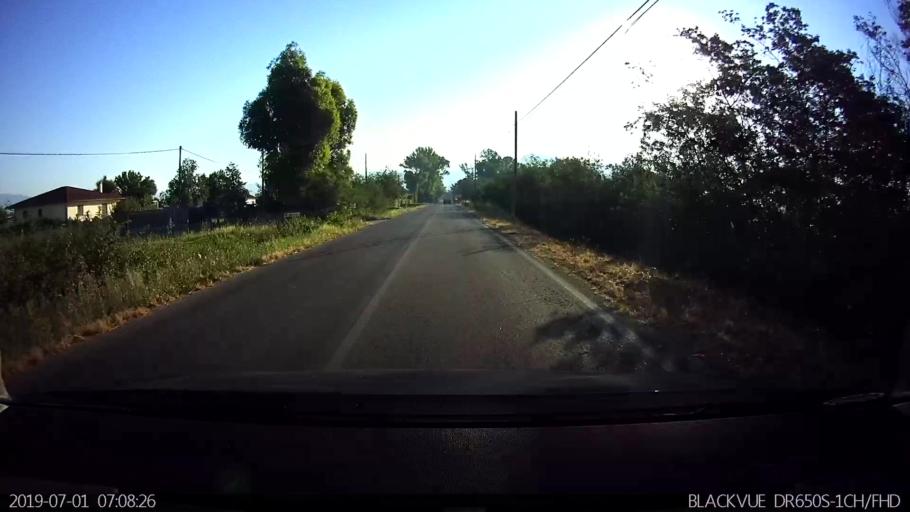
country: IT
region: Latium
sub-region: Provincia di Latina
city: Borgo Hermada
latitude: 41.2972
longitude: 13.1500
